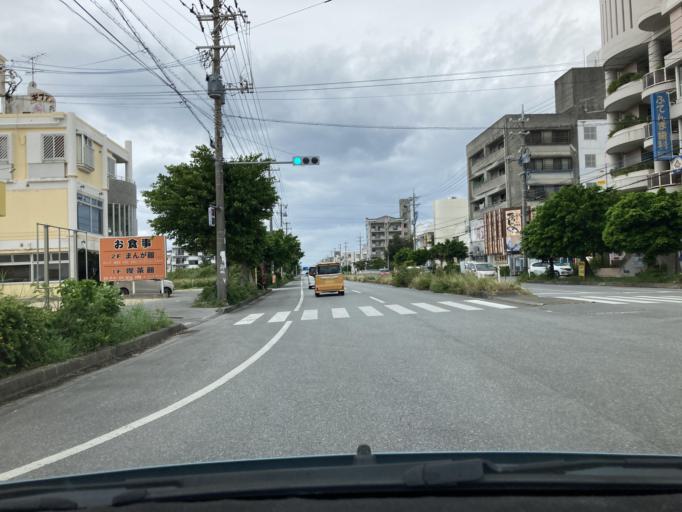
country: JP
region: Okinawa
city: Itoman
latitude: 26.1415
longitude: 127.6702
